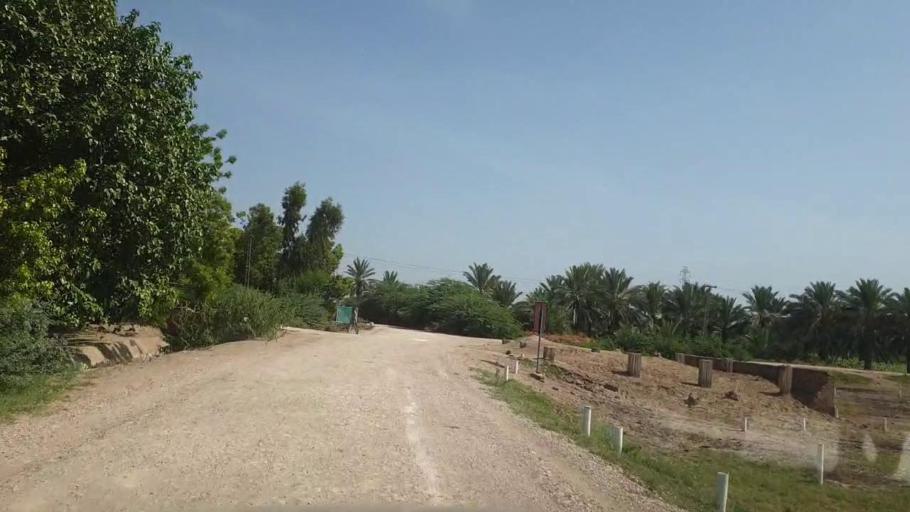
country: PK
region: Sindh
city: Rohri
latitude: 27.6669
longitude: 68.8832
